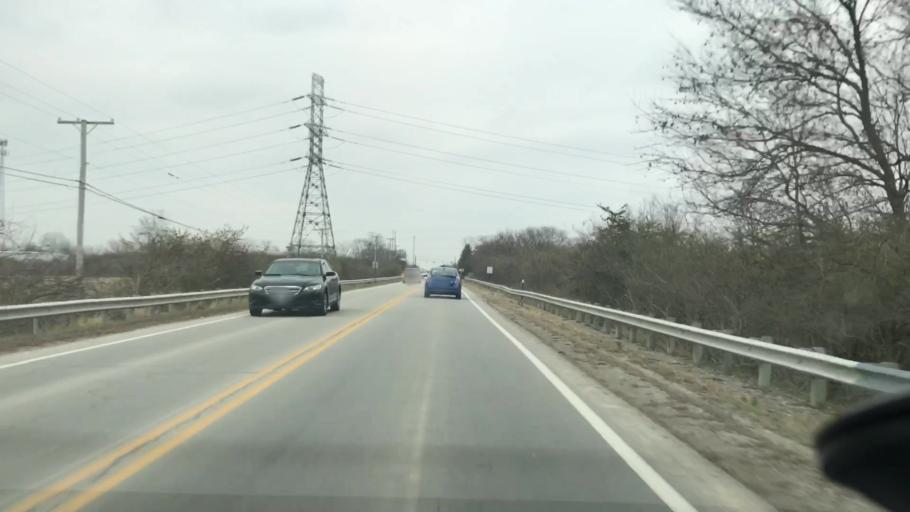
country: US
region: Ohio
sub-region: Greene County
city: Fairborn
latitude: 39.7864
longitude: -83.9784
